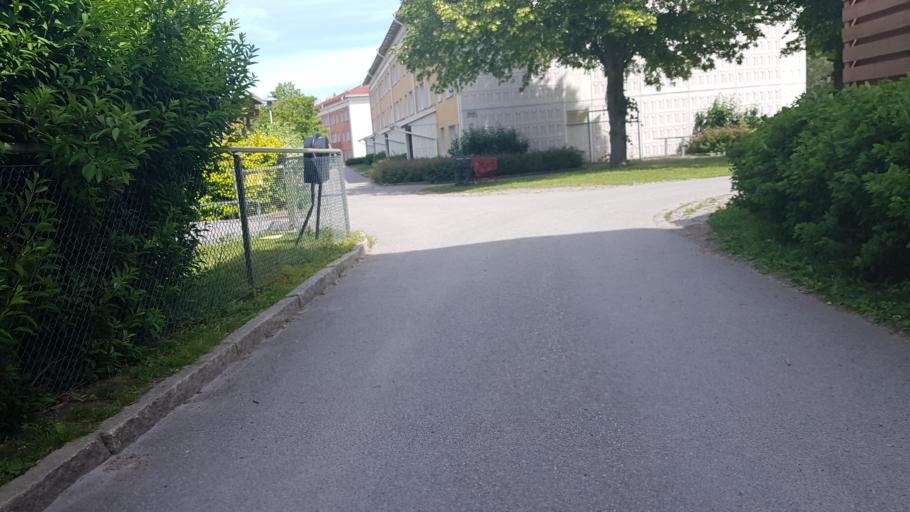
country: SE
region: OEstergoetland
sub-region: Norrkopings Kommun
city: Norrkoping
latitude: 58.5761
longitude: 16.2085
